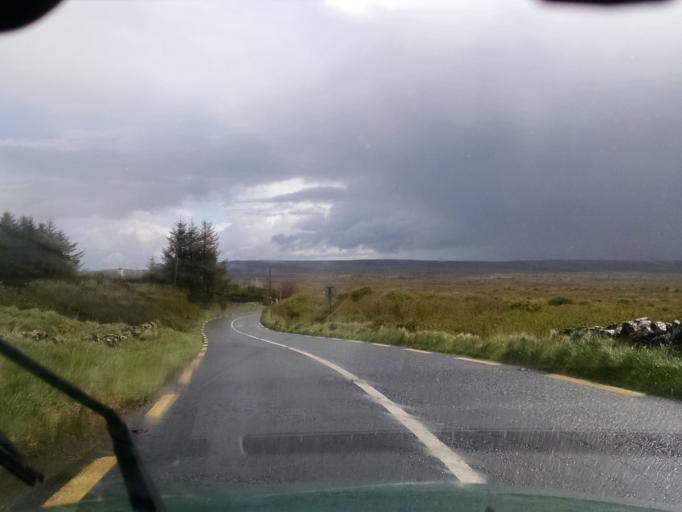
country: IE
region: Connaught
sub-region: County Galway
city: Bearna
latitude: 53.0625
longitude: -9.1941
